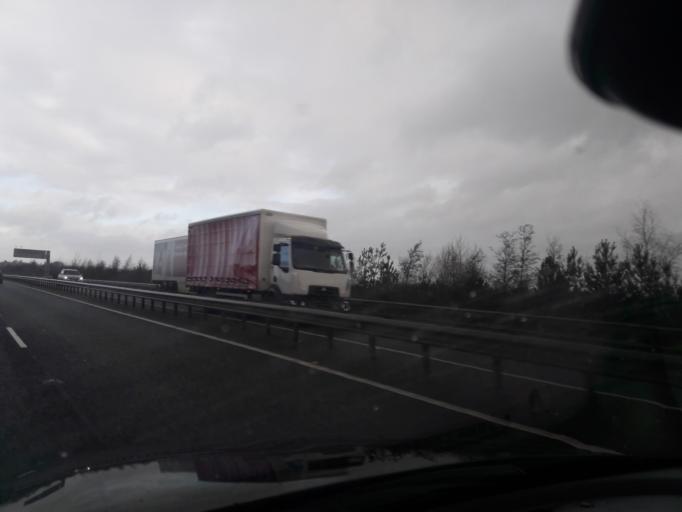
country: IE
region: Leinster
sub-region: An Mhi
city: Ashbourne
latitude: 53.5012
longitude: -6.4182
